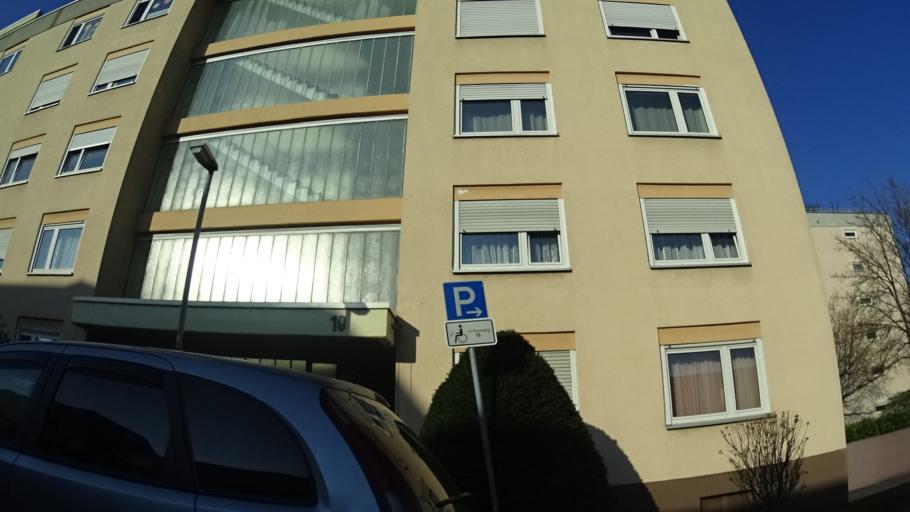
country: DE
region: Baden-Wuerttemberg
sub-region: Karlsruhe Region
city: Leimen
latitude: 49.3746
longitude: 8.6825
